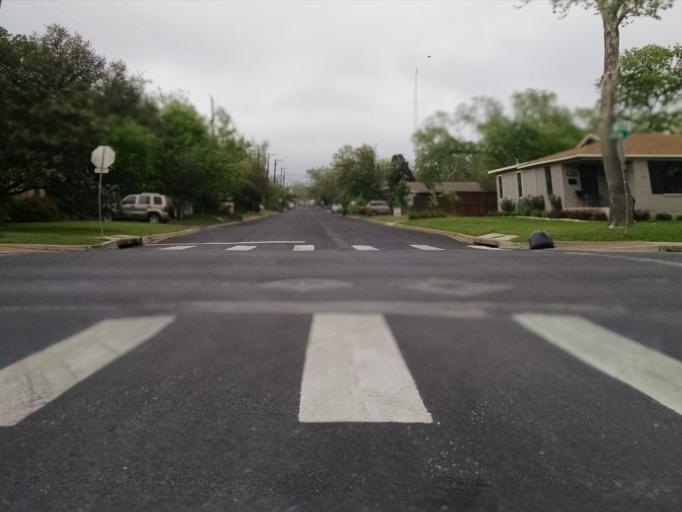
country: US
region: Texas
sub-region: Travis County
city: Austin
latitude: 30.3391
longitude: -97.7239
